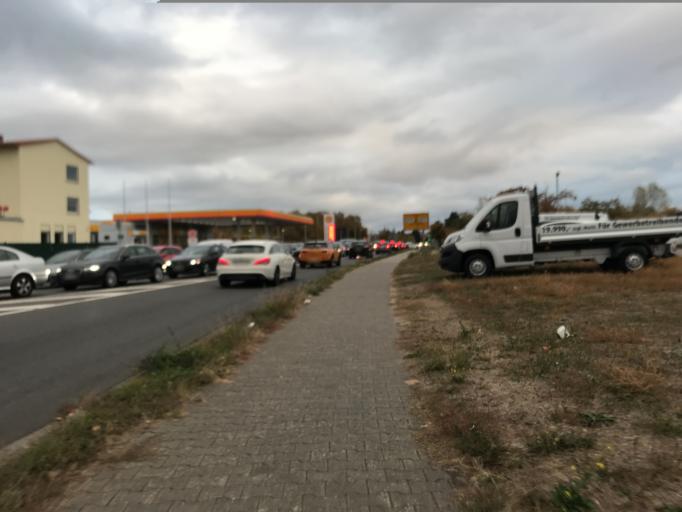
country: DE
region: Rheinland-Pfalz
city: Gau-Algesheim
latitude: 49.9711
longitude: 8.0211
